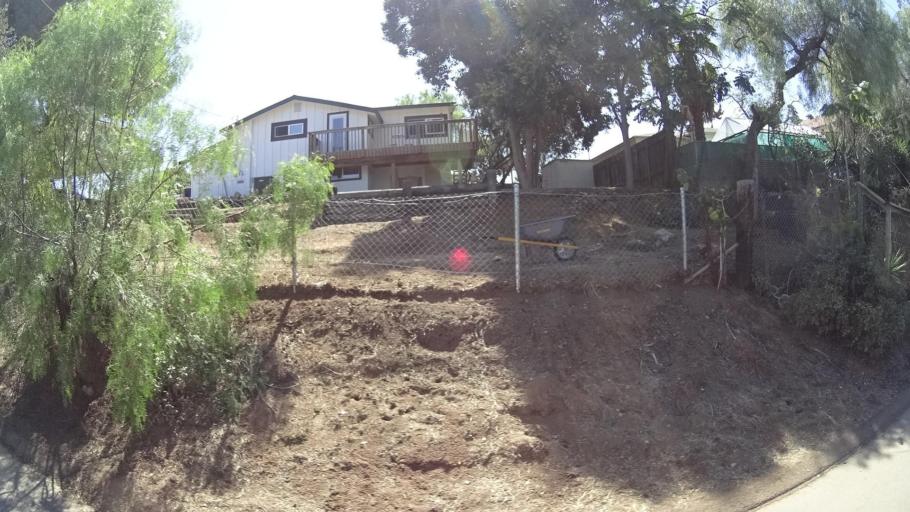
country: US
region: California
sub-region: San Diego County
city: Crest
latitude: 32.8073
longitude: -116.8677
